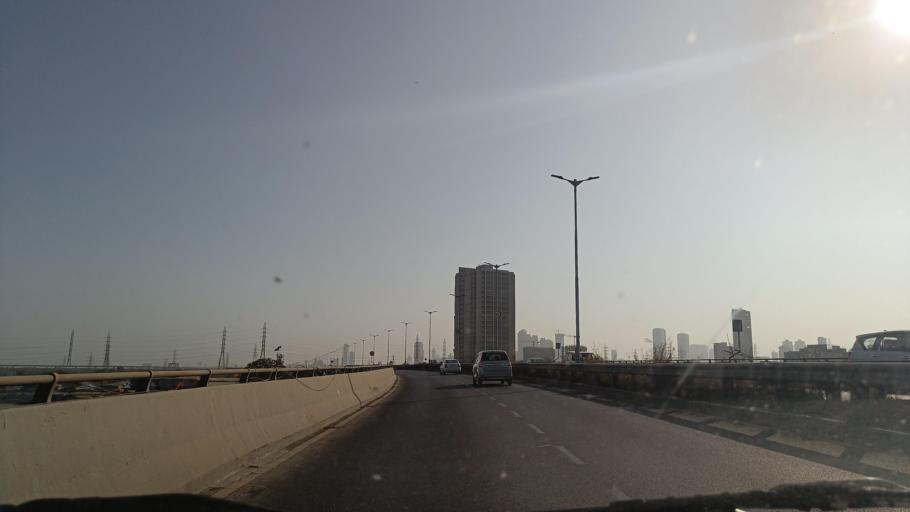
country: IN
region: Maharashtra
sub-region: Mumbai Suburban
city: Mumbai
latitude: 19.0230
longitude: 72.8768
